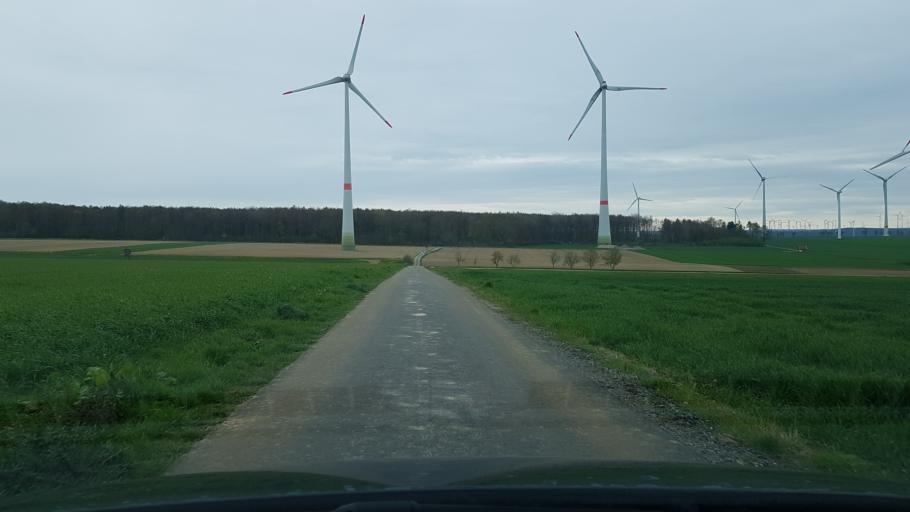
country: DE
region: North Rhine-Westphalia
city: Lichtenau
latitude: 51.6319
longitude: 8.8162
